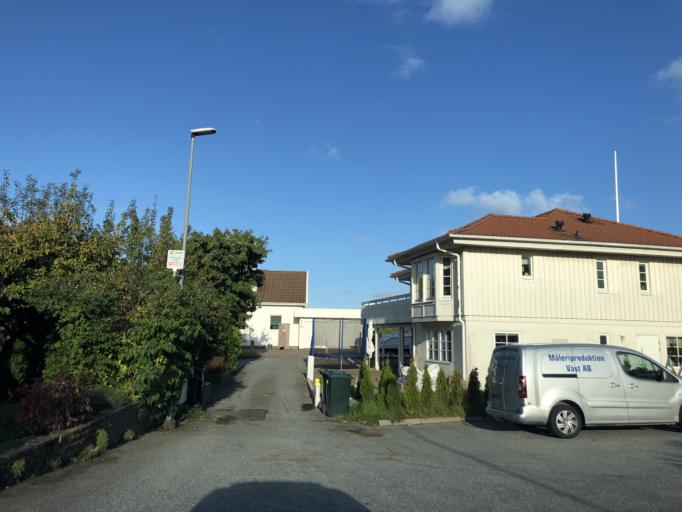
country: SE
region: Vaestra Goetaland
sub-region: Goteborg
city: Majorna
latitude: 57.6406
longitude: 11.8715
